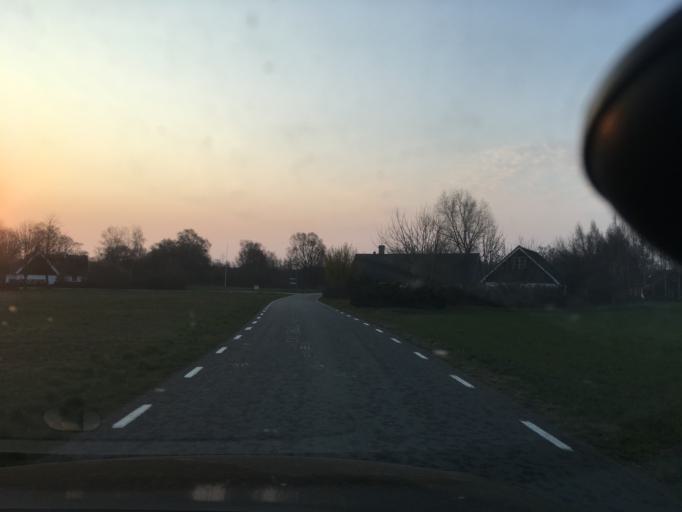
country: SE
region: Skane
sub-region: Ystads Kommun
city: Kopingebro
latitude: 55.4003
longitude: 14.1647
